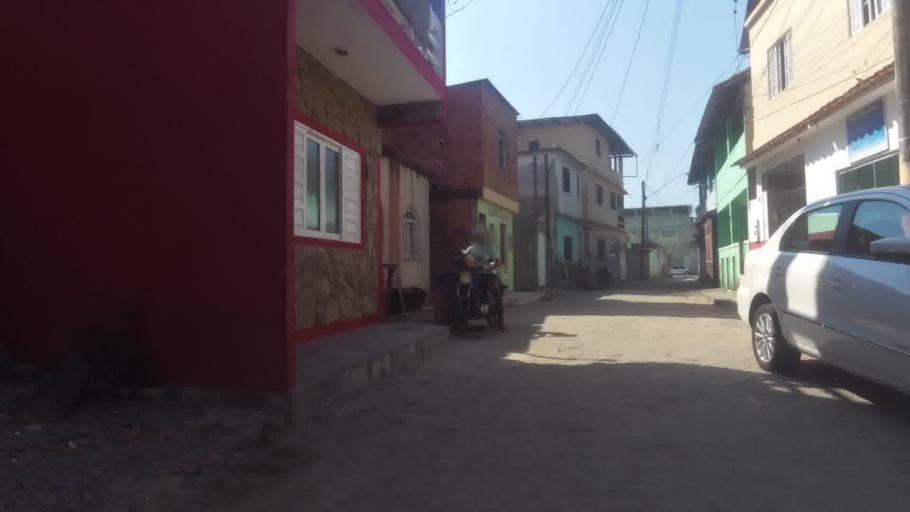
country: BR
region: Espirito Santo
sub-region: Itapemirim
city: Itapemirim
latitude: -21.0122
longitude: -40.8129
